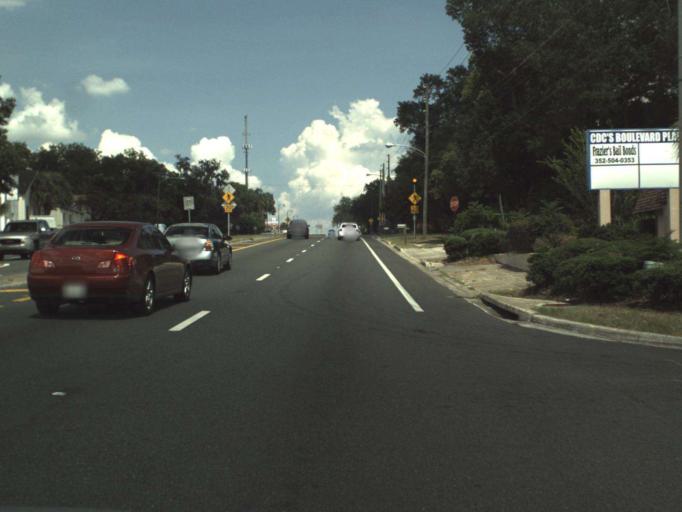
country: US
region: Florida
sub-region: Lake County
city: Leesburg
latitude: 28.8134
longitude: -81.8627
